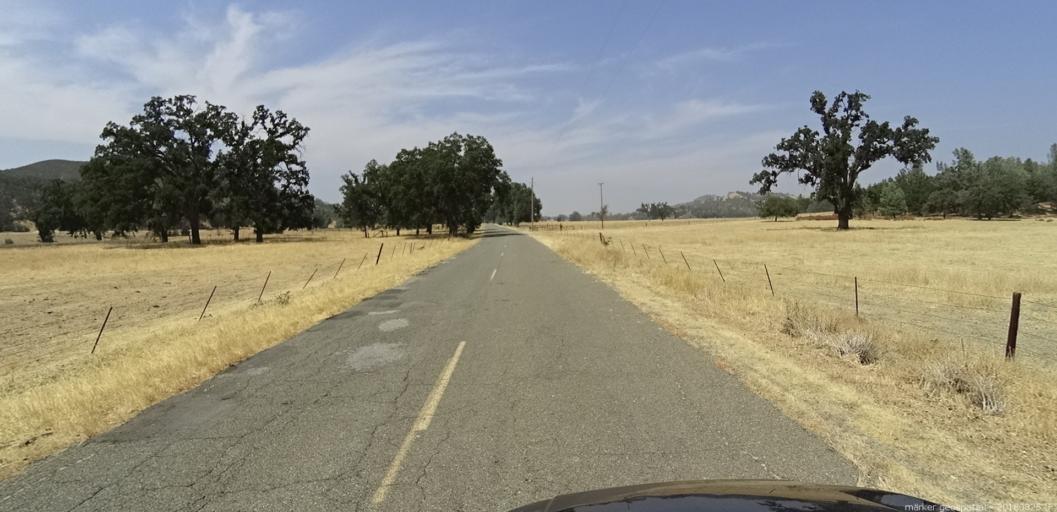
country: US
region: California
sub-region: Fresno County
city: Coalinga
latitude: 35.9208
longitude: -120.4927
